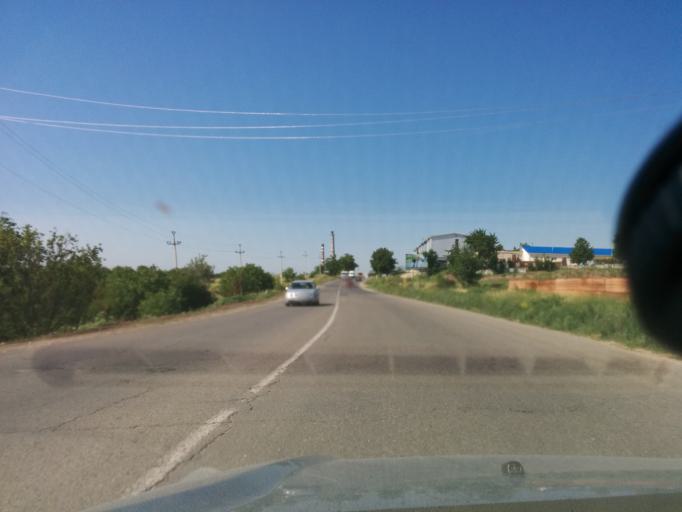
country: MD
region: Chisinau
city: Chisinau
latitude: 47.0448
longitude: 28.9085
